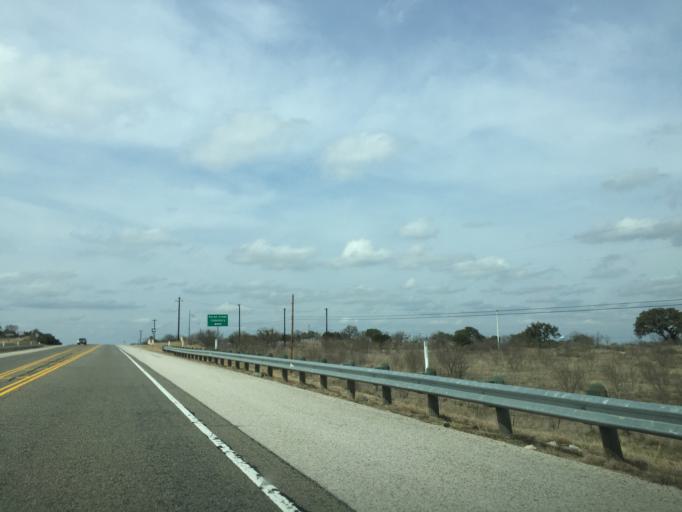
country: US
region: Texas
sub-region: Burnet County
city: Granite Shoals
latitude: 30.5186
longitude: -98.4076
